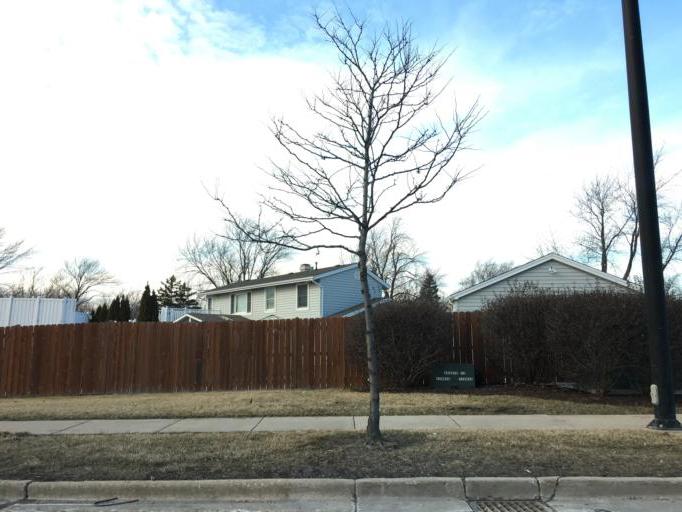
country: US
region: Illinois
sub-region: Cook County
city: Schaumburg
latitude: 42.0267
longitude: -88.0980
